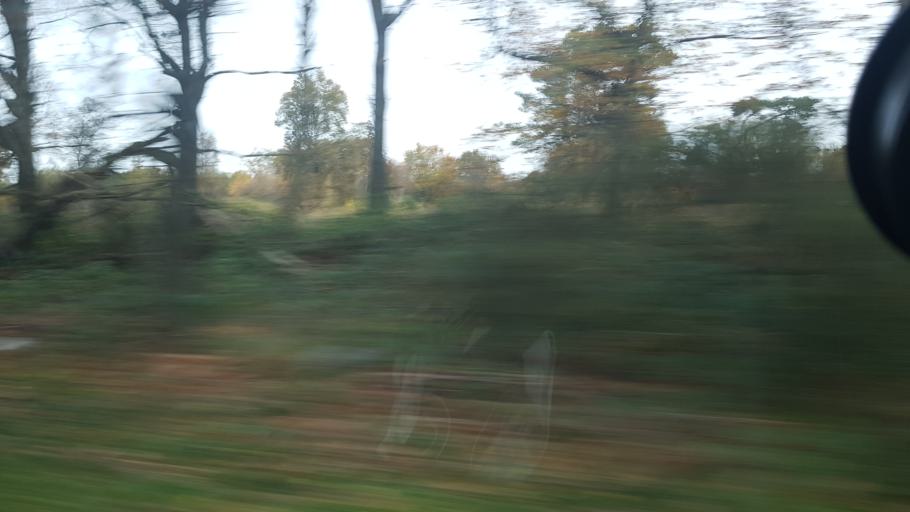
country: GB
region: England
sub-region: Hampshire
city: Yateley
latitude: 51.3226
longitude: -0.8355
